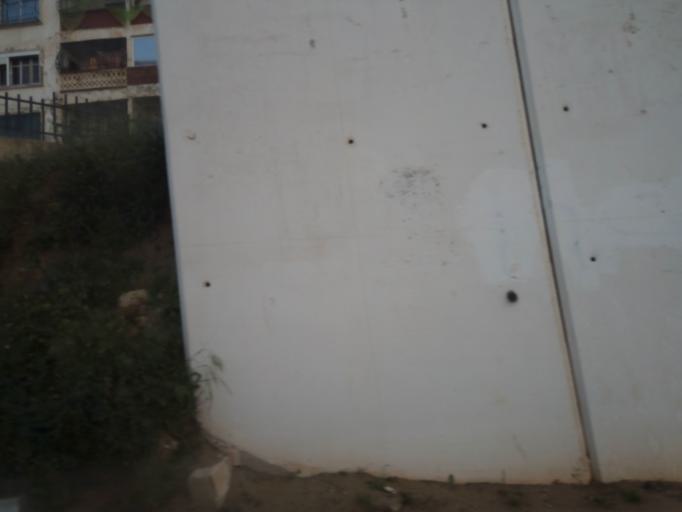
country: DZ
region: Tipaza
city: Bou Ismail
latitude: 36.6205
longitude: 2.6507
